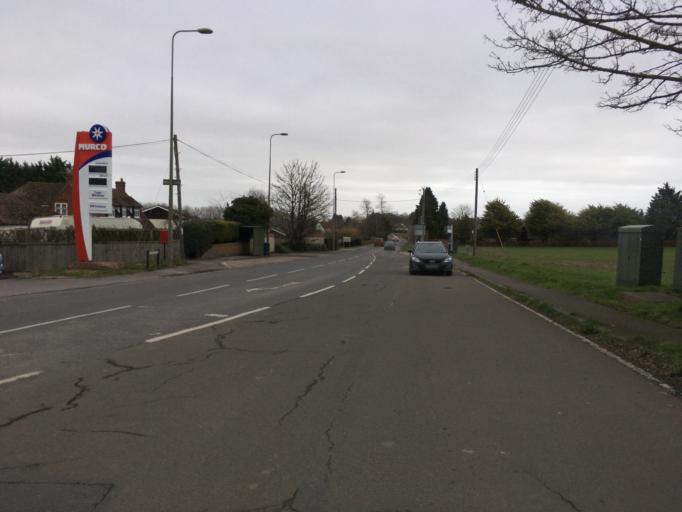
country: GB
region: England
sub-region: Oxfordshire
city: Harwell
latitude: 51.5994
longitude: -1.3100
